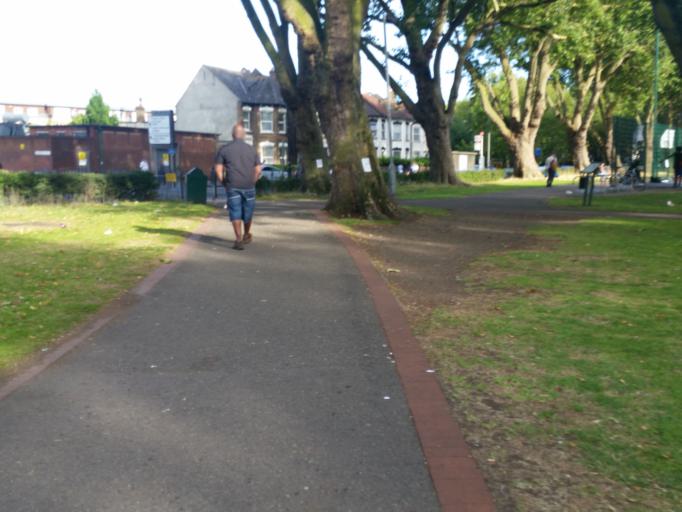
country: GB
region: England
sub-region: Greater London
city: Harringay
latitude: 51.5896
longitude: -0.1030
